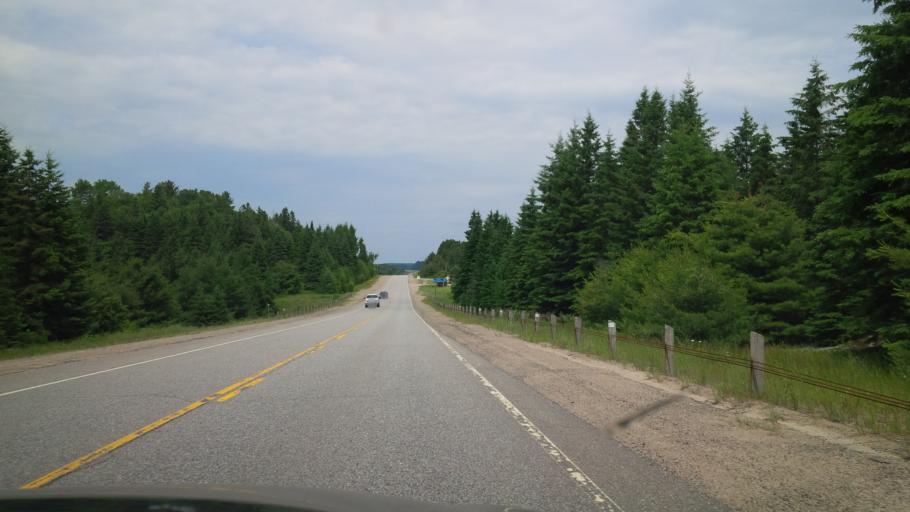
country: CA
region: Ontario
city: Huntsville
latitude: 45.5204
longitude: -79.3140
